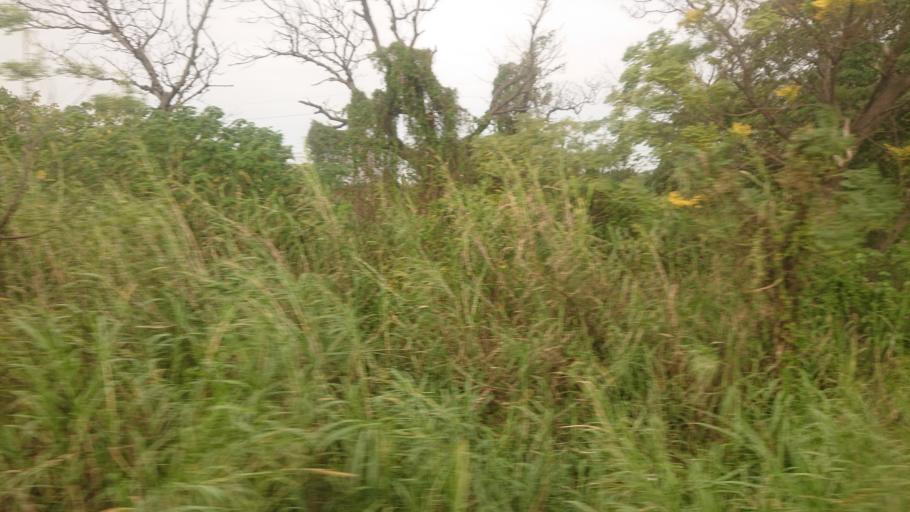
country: TW
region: Taiwan
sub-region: Changhua
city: Chang-hua
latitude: 24.1148
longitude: 120.5811
